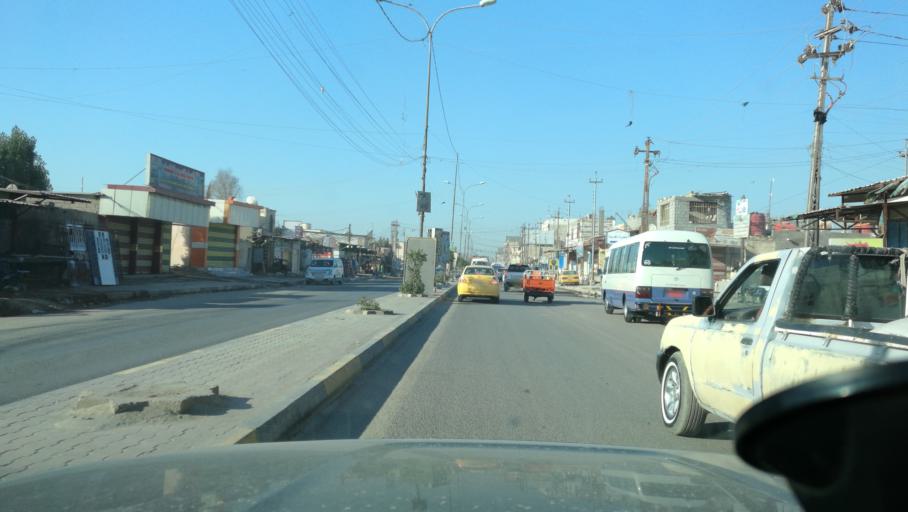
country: IQ
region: Basra Governorate
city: Al Basrah al Qadimah
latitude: 30.4930
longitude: 47.8176
